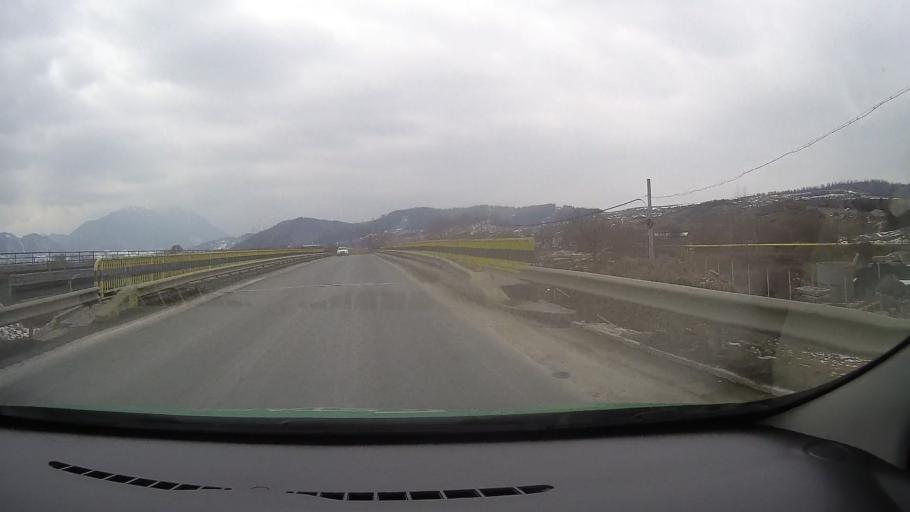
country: RO
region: Brasov
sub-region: Comuna Zarnesti
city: Tohanu Nou
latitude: 45.5773
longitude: 25.3919
